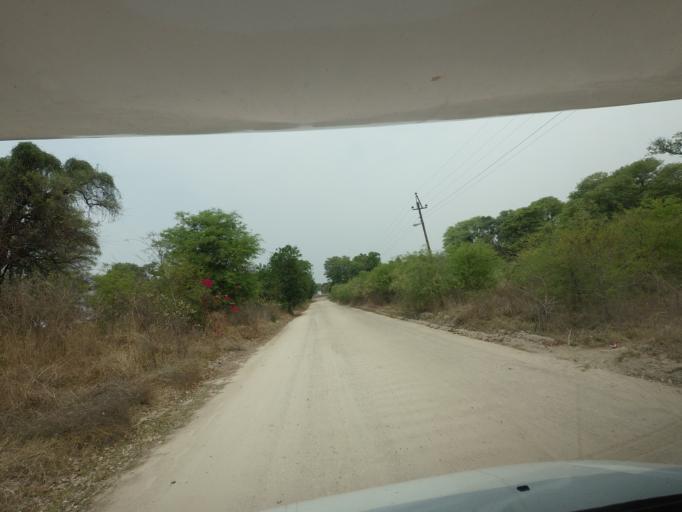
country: ZM
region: Western
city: Sesheke
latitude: -17.4876
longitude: 24.2852
